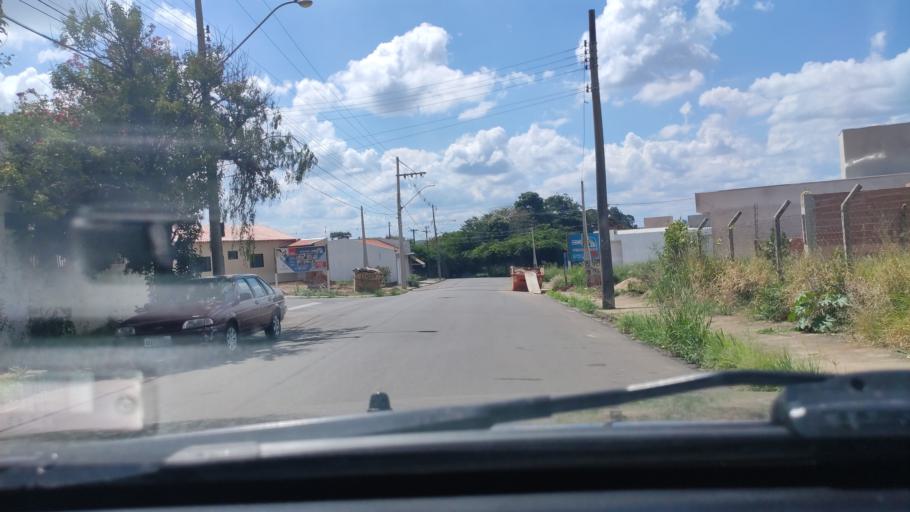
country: BR
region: Sao Paulo
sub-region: Sao Carlos
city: Sao Carlos
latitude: -21.9975
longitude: -47.8782
